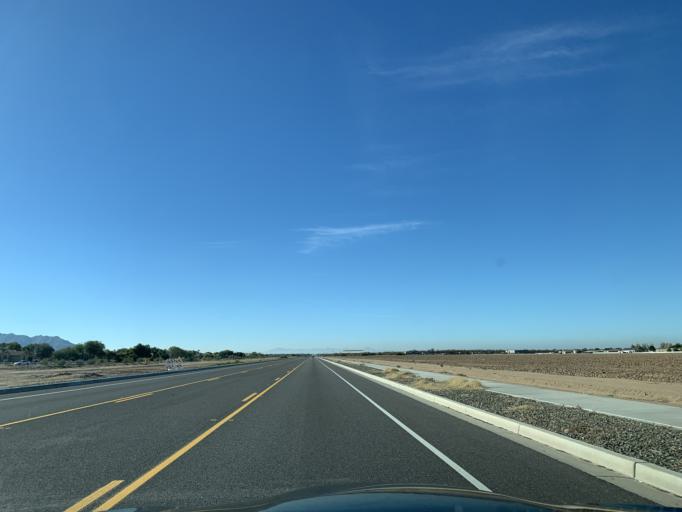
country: US
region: Arizona
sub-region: Maricopa County
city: Queen Creek
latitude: 33.2196
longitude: -111.6197
